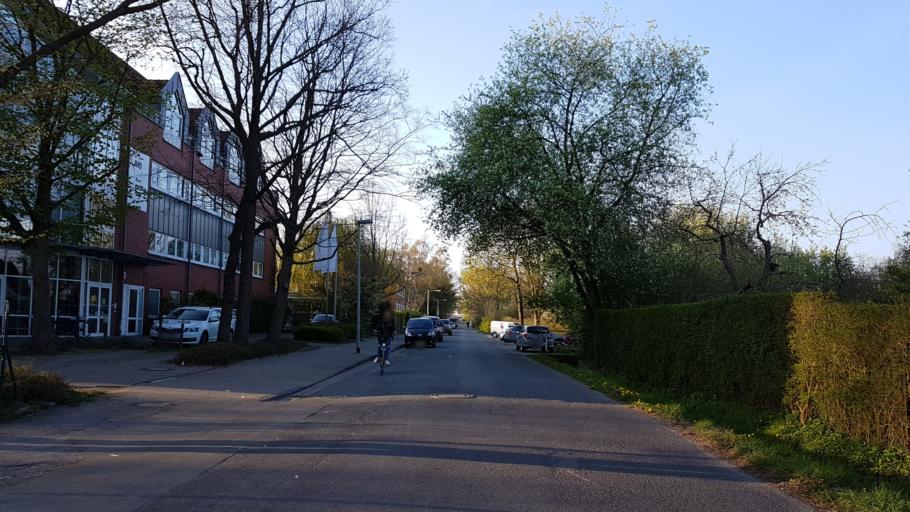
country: DE
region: Lower Saxony
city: Hannover
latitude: 52.3567
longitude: 9.6875
